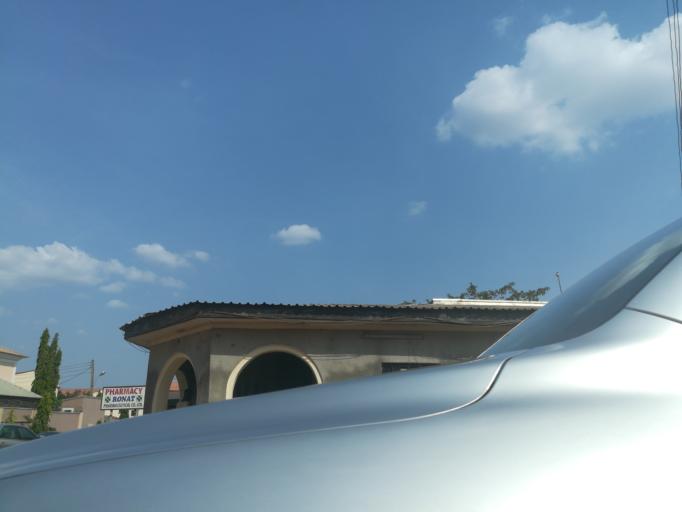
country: NG
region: Abuja Federal Capital Territory
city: Abuja
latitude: 9.0800
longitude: 7.4121
